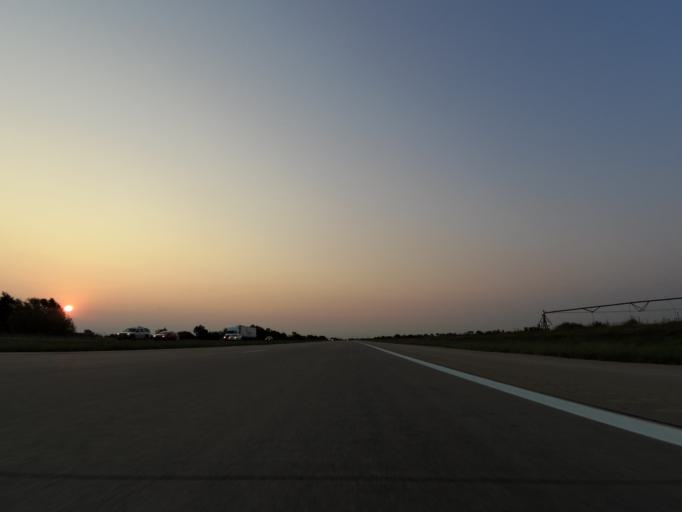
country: US
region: Kansas
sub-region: Reno County
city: South Hutchinson
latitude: 37.9532
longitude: -97.8986
